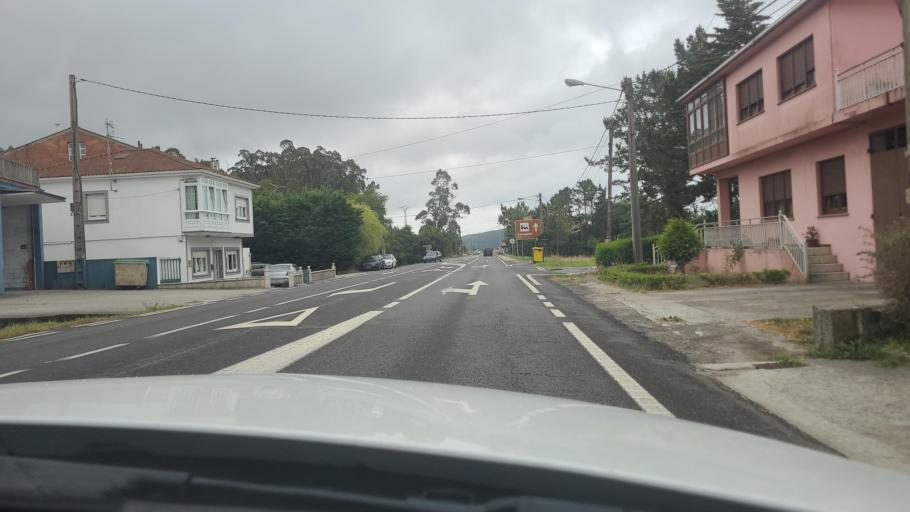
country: ES
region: Galicia
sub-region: Provincia da Coruna
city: Cee
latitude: 42.9808
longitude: -9.1873
